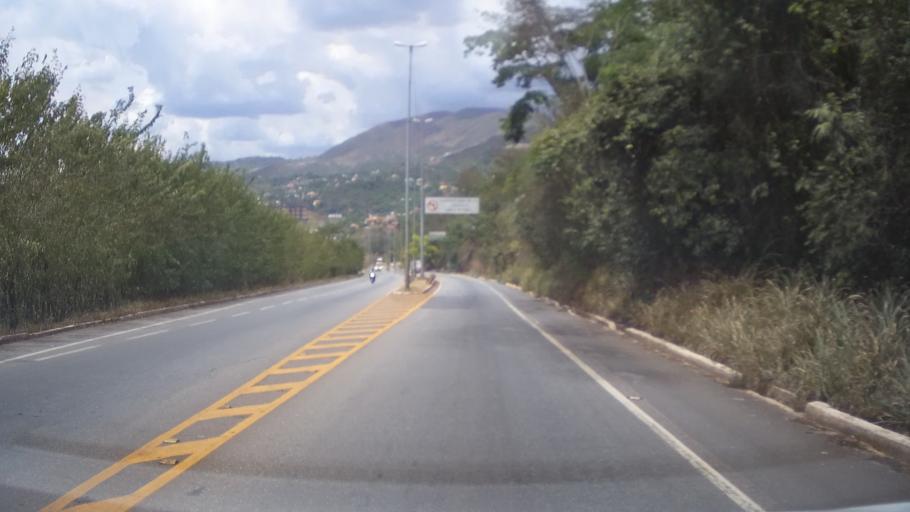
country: BR
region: Minas Gerais
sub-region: Nova Lima
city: Nova Lima
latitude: -19.9936
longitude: -43.8579
